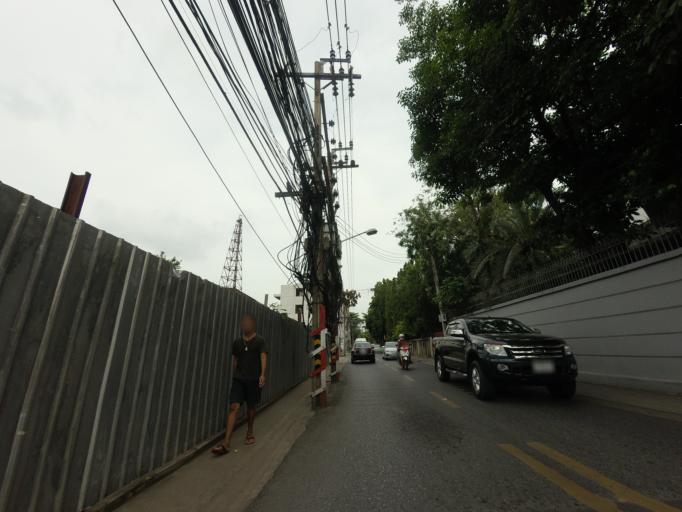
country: TH
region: Bangkok
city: Watthana
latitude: 13.7463
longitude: 100.5890
